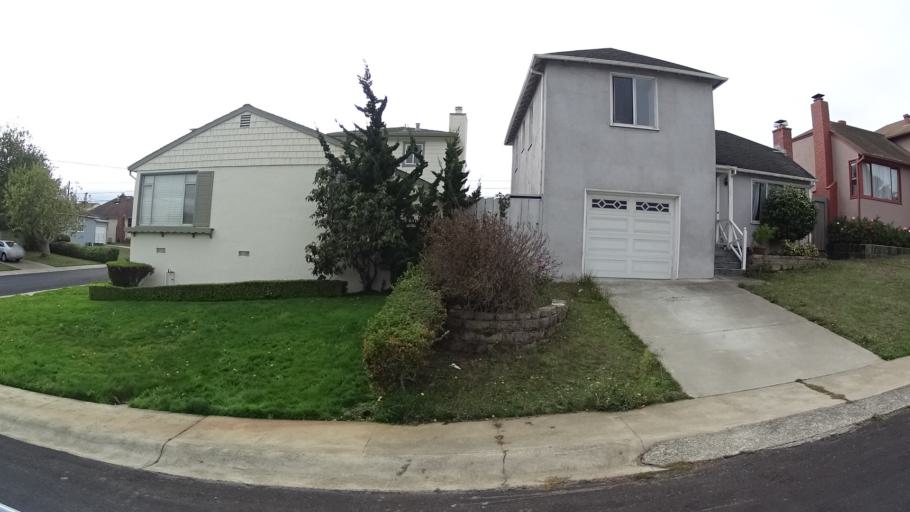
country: US
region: California
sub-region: San Mateo County
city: South San Francisco
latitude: 37.6523
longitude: -122.4339
